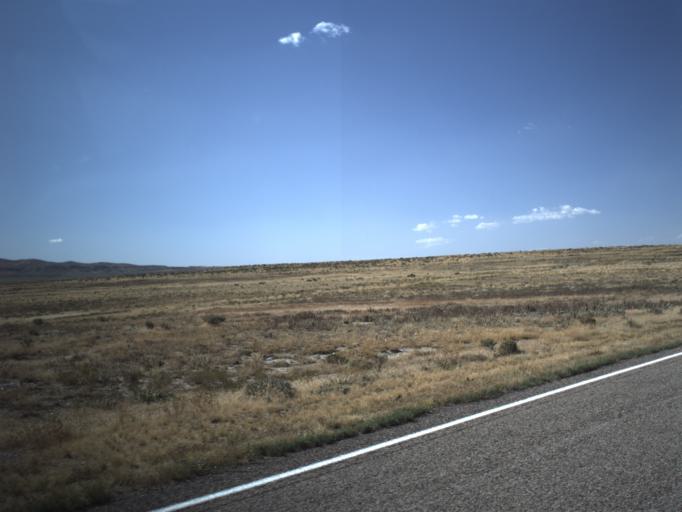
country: US
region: Utah
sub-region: Beaver County
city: Milford
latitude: 38.8120
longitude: -112.8691
